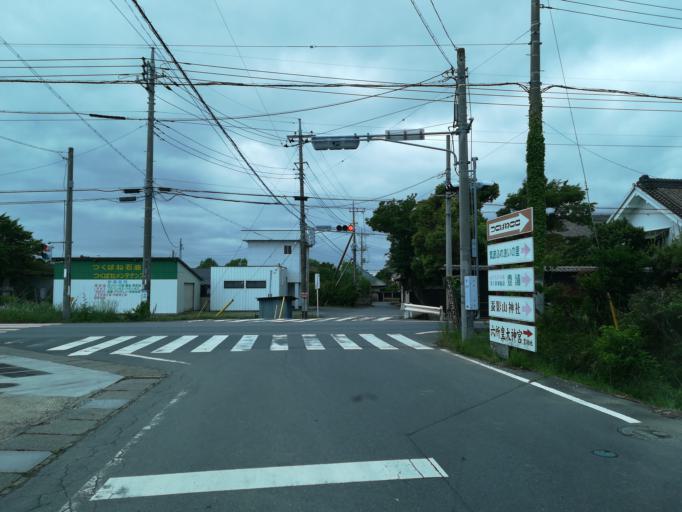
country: JP
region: Ibaraki
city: Tsukuba
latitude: 36.1946
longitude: 140.0788
